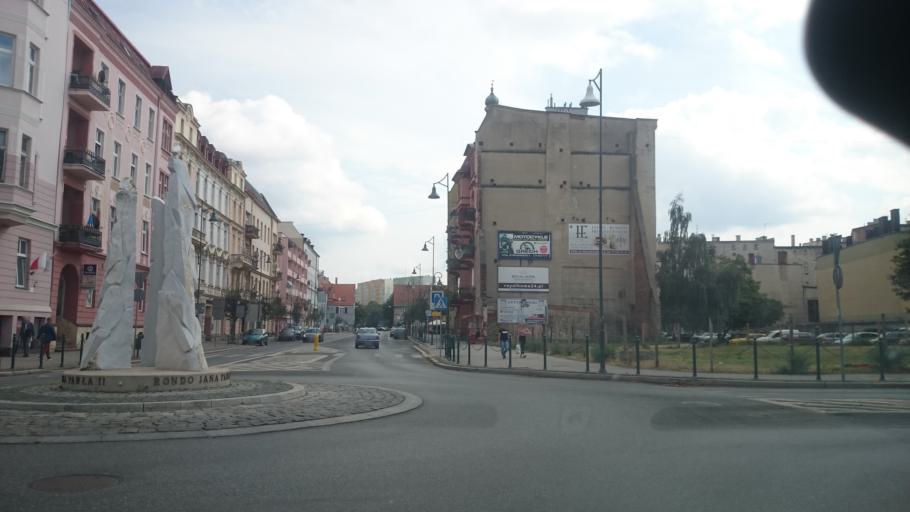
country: PL
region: Opole Voivodeship
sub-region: Powiat nyski
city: Nysa
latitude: 50.4708
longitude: 17.3363
